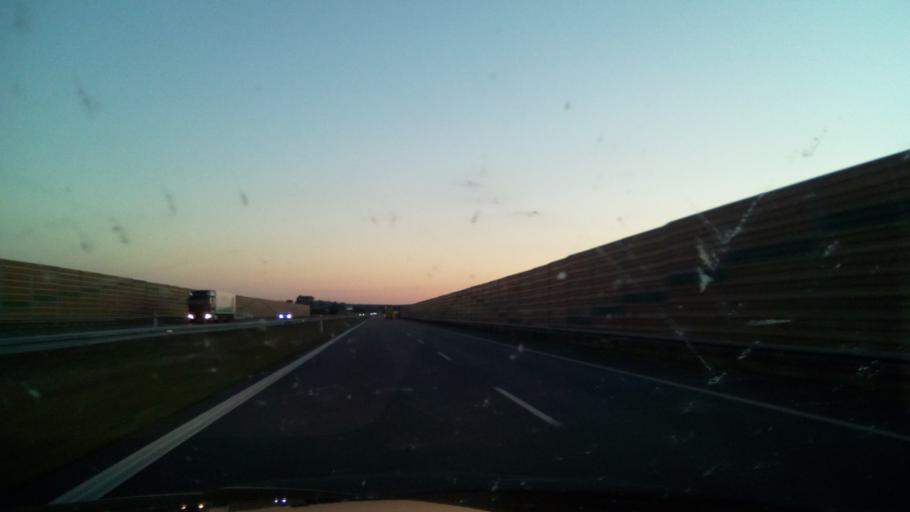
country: PL
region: Greater Poland Voivodeship
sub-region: Powiat koninski
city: Krzymow
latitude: 52.1480
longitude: 18.4305
